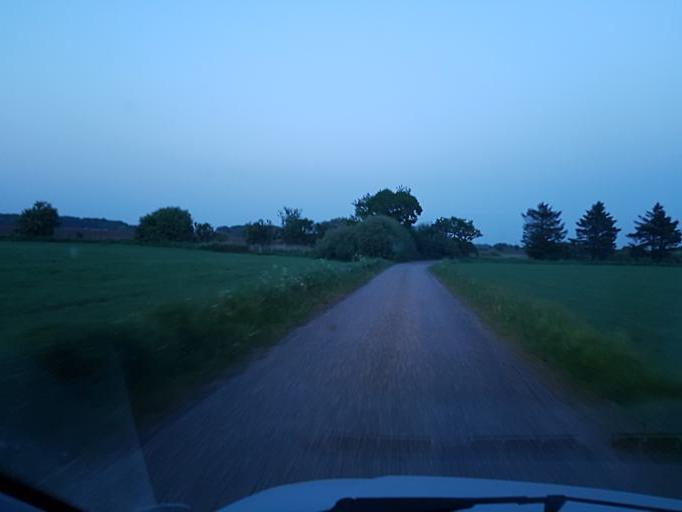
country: DK
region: South Denmark
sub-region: Esbjerg Kommune
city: Tjaereborg
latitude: 55.5099
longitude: 8.5713
